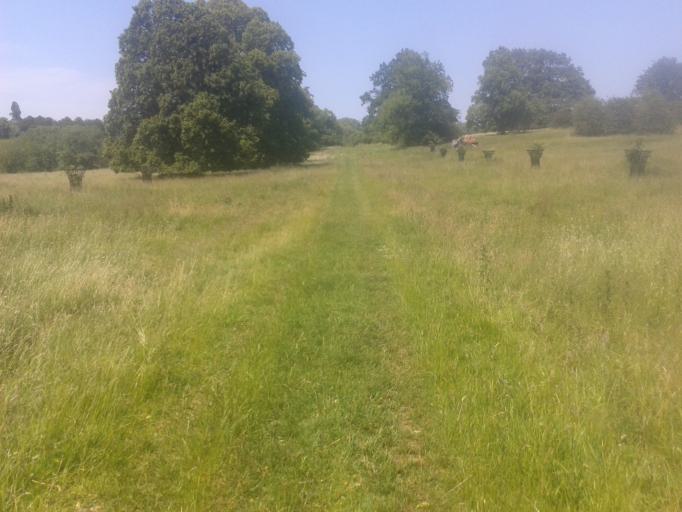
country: GB
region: England
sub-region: East Riding of Yorkshire
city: Londesborough
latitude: 53.8945
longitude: -0.6719
